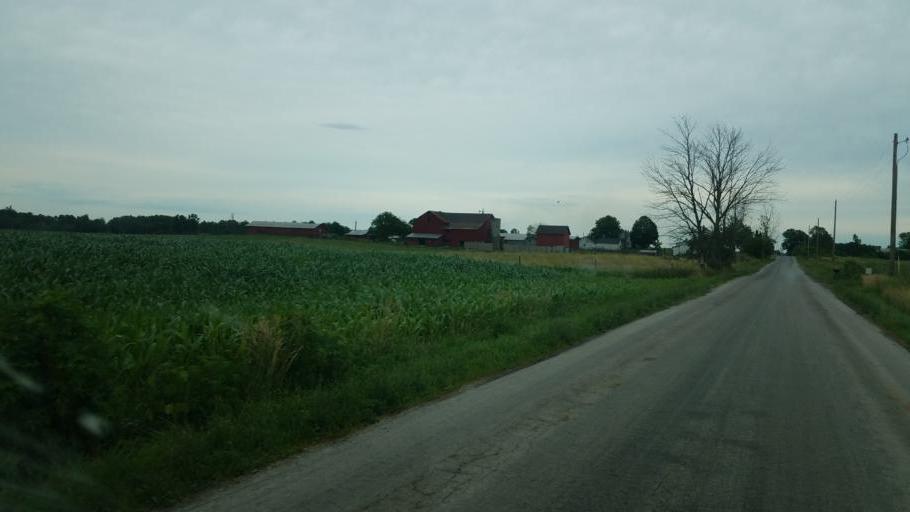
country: US
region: Ohio
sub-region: Ashland County
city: Ashland
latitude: 40.9314
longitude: -82.4176
